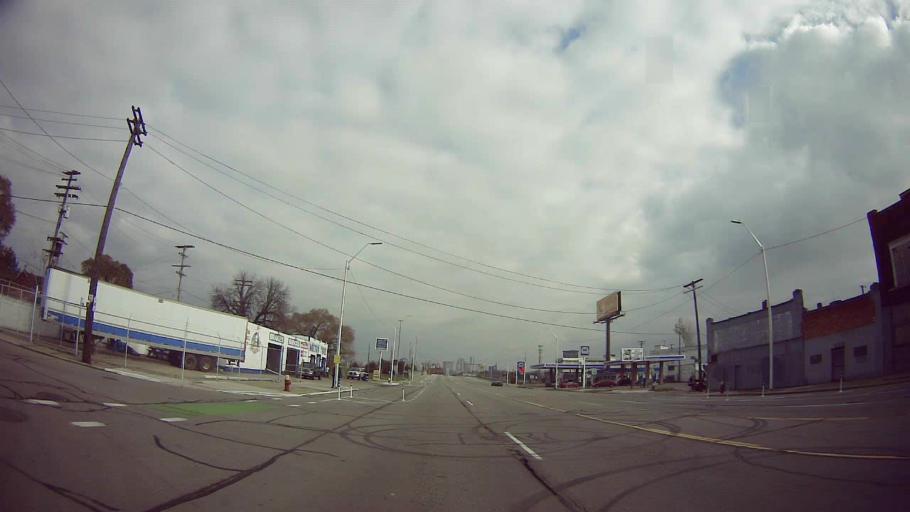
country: US
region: Michigan
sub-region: Wayne County
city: Detroit
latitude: 42.3315
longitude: -83.0894
